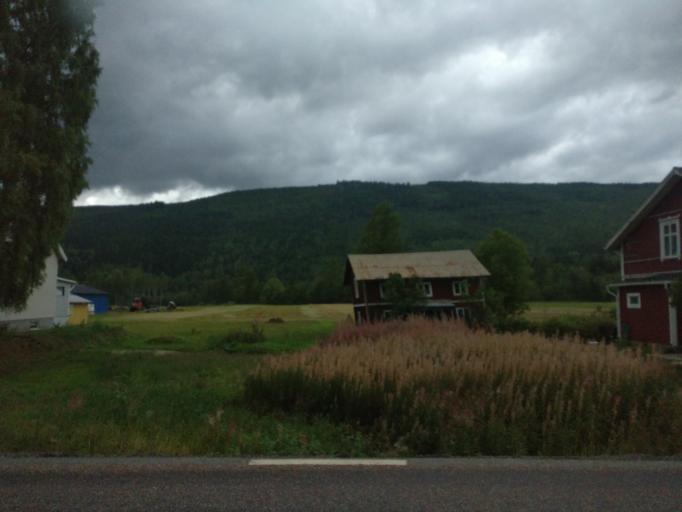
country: SE
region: Vaermland
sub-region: Torsby Kommun
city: Torsby
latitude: 60.7085
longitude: 12.8923
